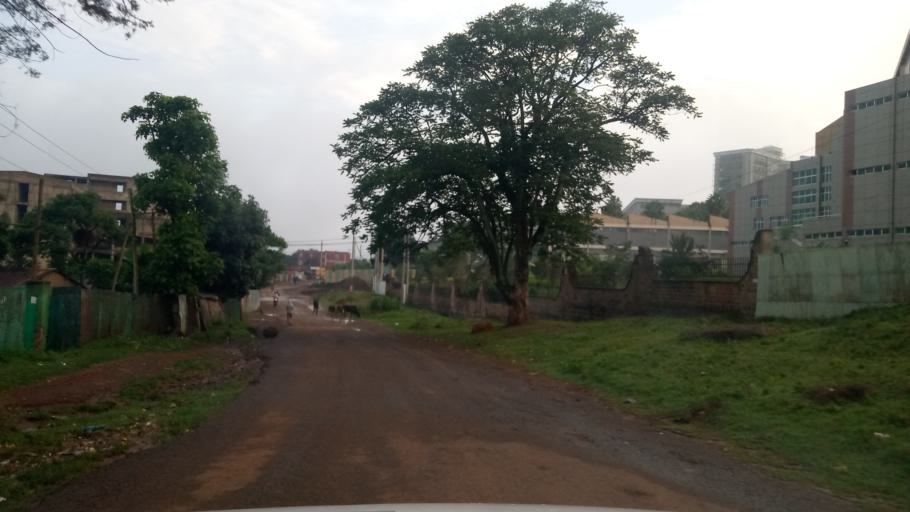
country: ET
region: Oromiya
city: Jima
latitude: 7.6807
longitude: 36.8507
